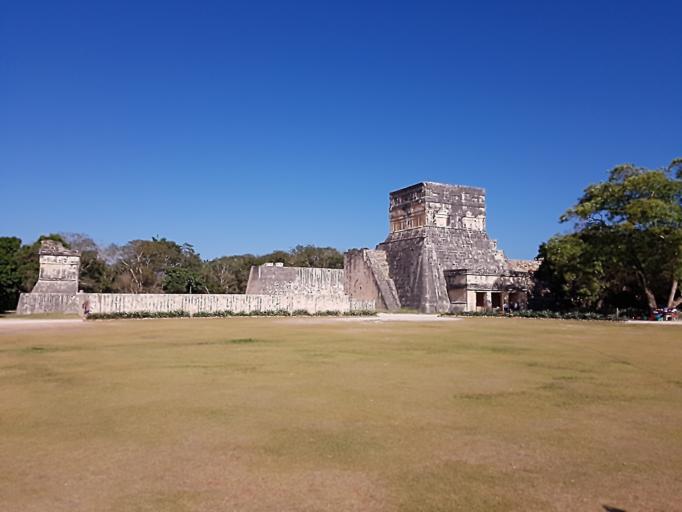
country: MX
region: Yucatan
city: Chichen-Itza
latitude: 20.6835
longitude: -88.5695
